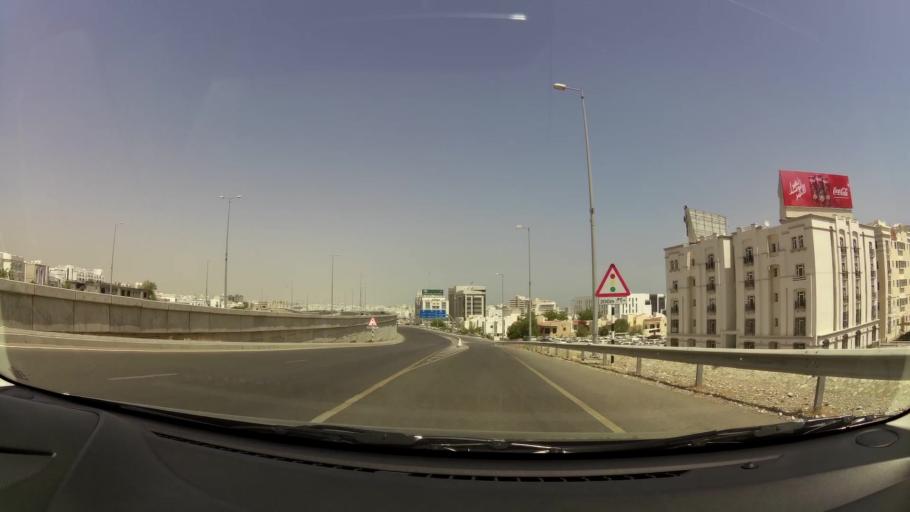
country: OM
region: Muhafazat Masqat
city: Bawshar
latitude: 23.5906
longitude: 58.4505
